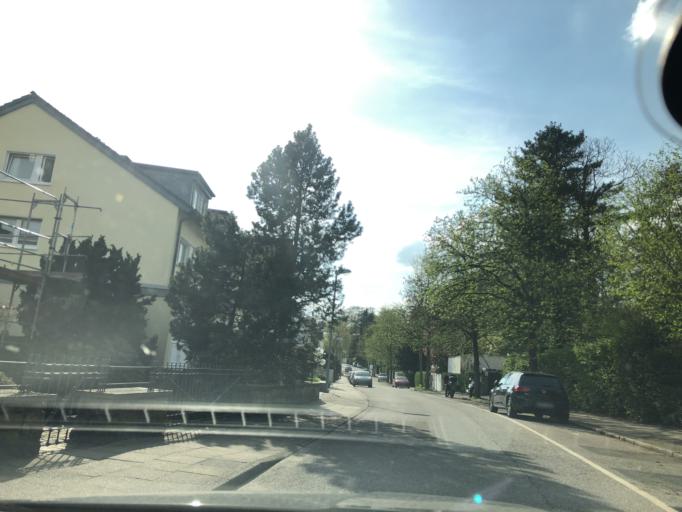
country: DE
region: North Rhine-Westphalia
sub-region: Regierungsbezirk Dusseldorf
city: Essen
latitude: 51.4132
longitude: 7.0604
